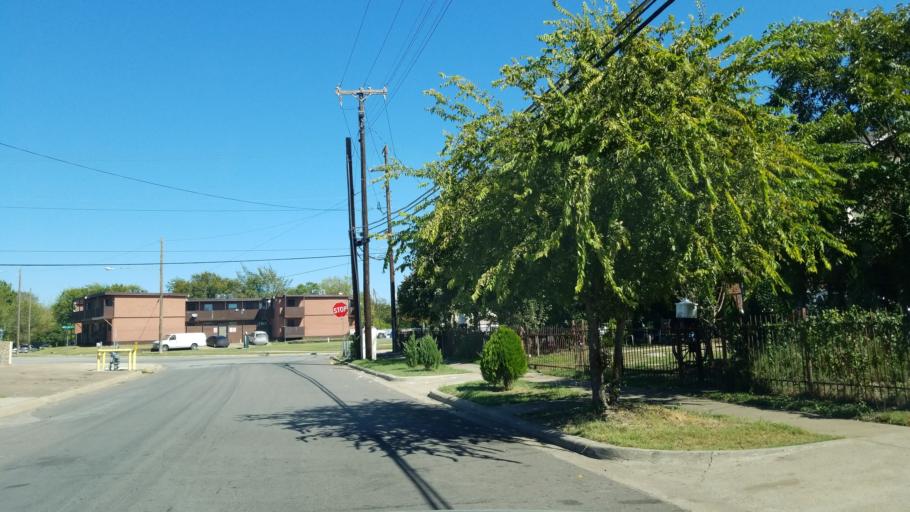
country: US
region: Texas
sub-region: Dallas County
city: Dallas
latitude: 32.7938
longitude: -96.7629
